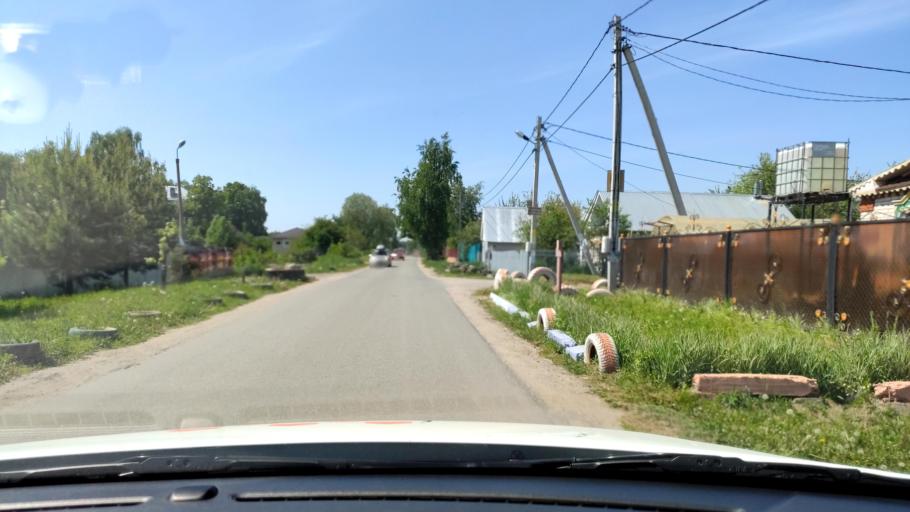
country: RU
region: Tatarstan
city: Osinovo
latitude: 55.8467
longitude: 48.8991
